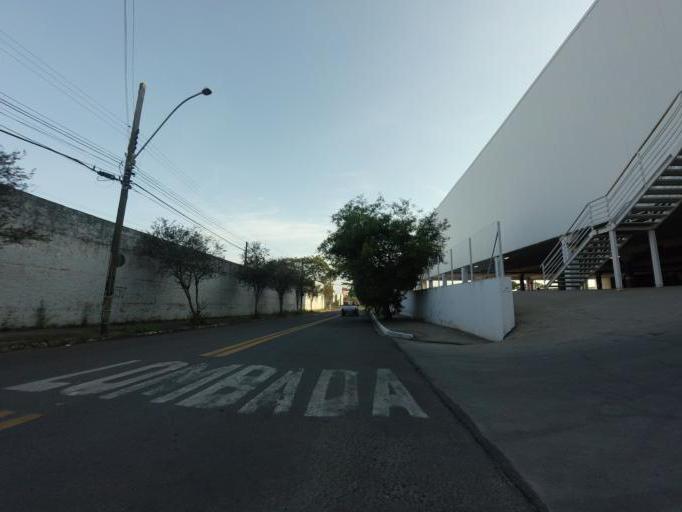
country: BR
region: Sao Paulo
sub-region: Piracicaba
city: Piracicaba
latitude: -22.7351
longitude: -47.6078
